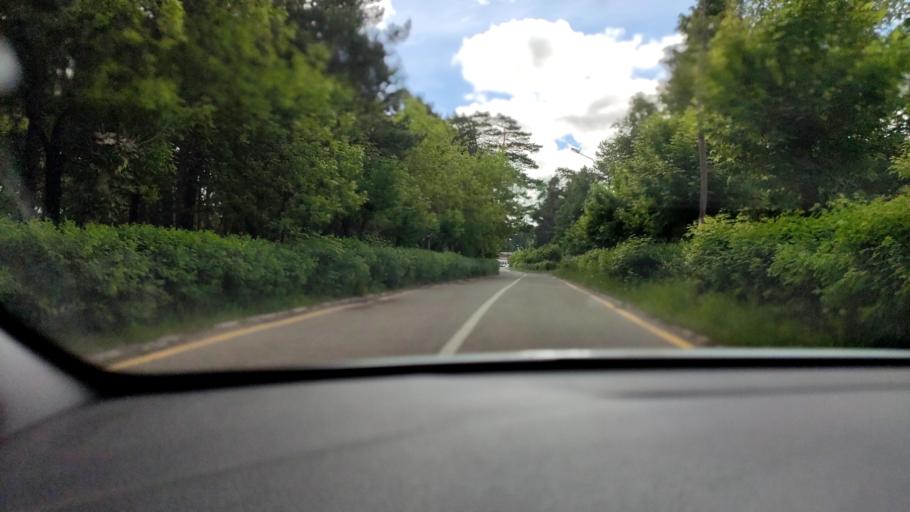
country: RU
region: Tatarstan
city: Vysokaya Gora
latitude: 55.8719
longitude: 49.2167
